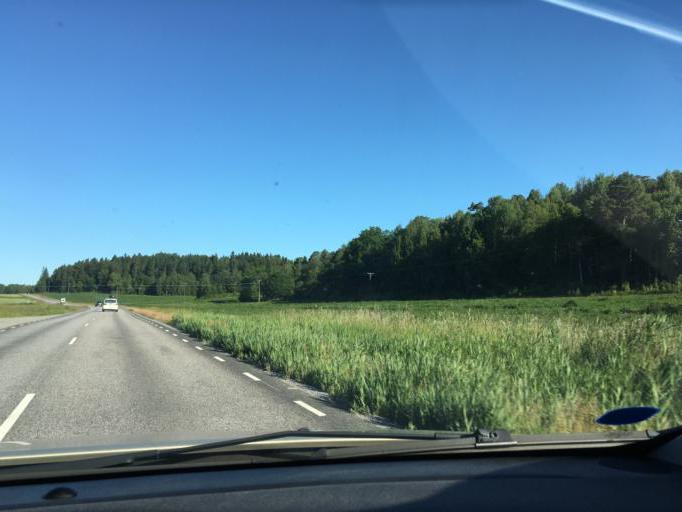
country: SE
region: Stockholm
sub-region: Salems Kommun
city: Ronninge
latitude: 59.2257
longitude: 17.7335
